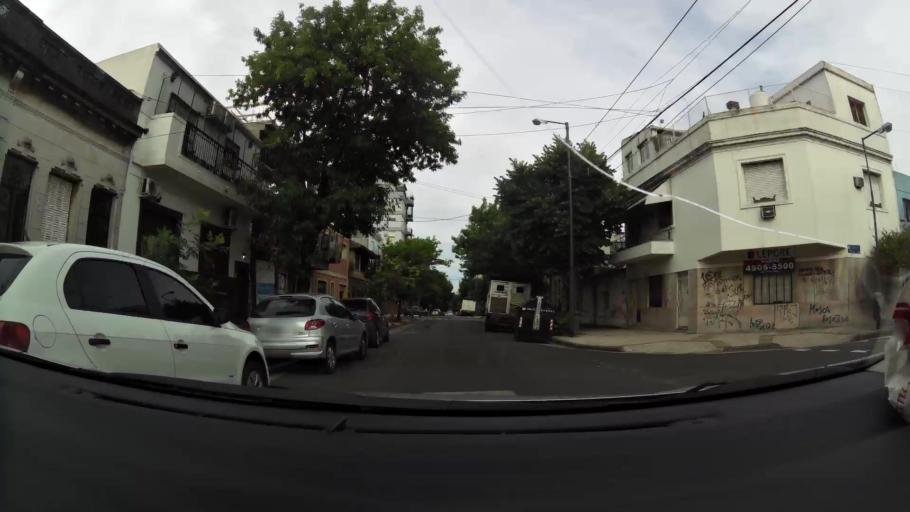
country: AR
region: Buenos Aires F.D.
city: Villa Santa Rita
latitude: -34.6300
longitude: -58.4311
